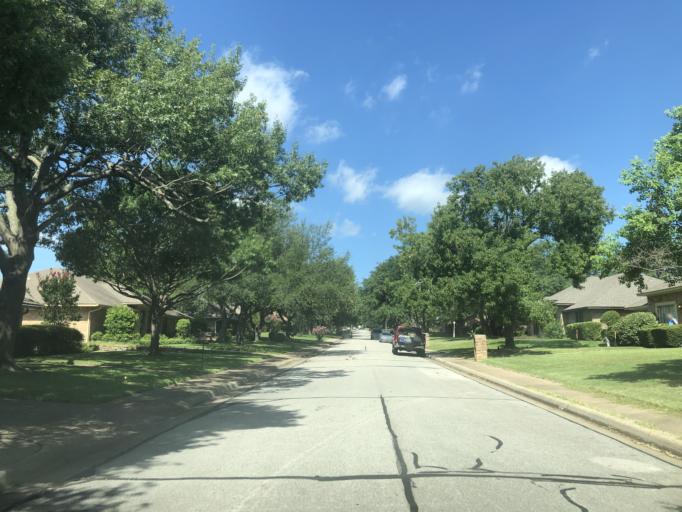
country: US
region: Texas
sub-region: Dallas County
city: Duncanville
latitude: 32.6479
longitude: -96.9300
